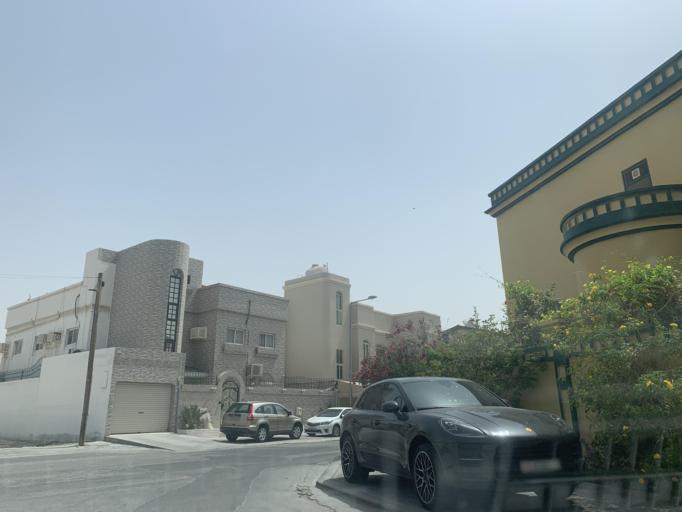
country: BH
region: Northern
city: Madinat `Isa
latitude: 26.1799
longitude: 50.5547
